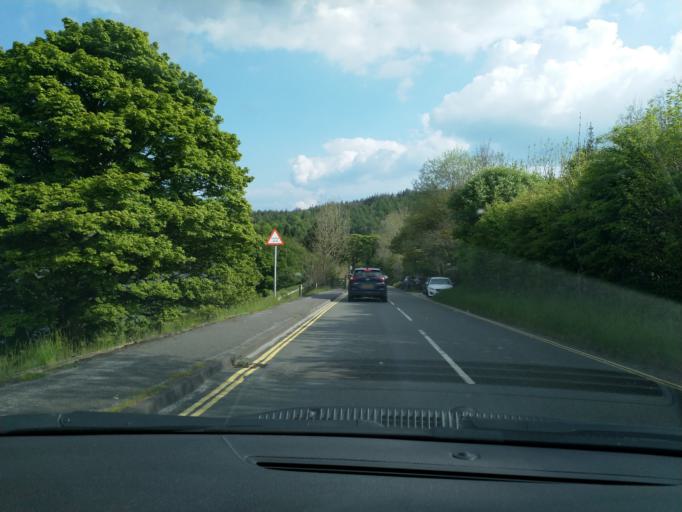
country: GB
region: England
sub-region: Derbyshire
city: Hope Valley
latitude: 53.3761
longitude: -1.7144
